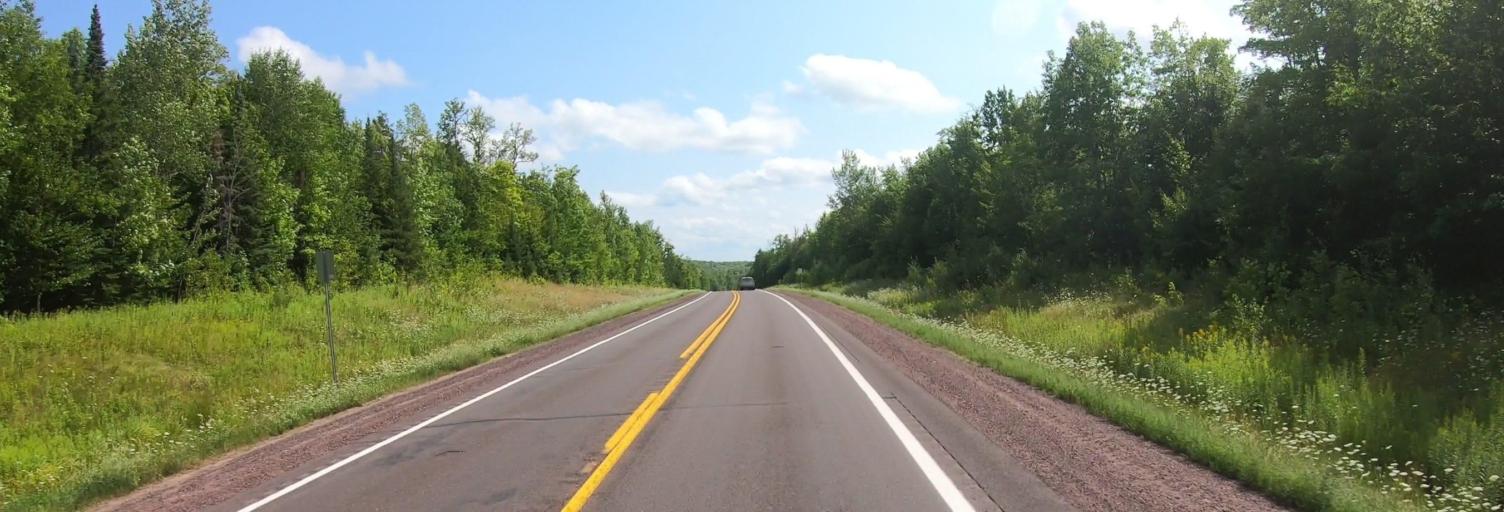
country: US
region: Michigan
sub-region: Ontonagon County
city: Ontonagon
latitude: 46.8224
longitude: -88.9970
